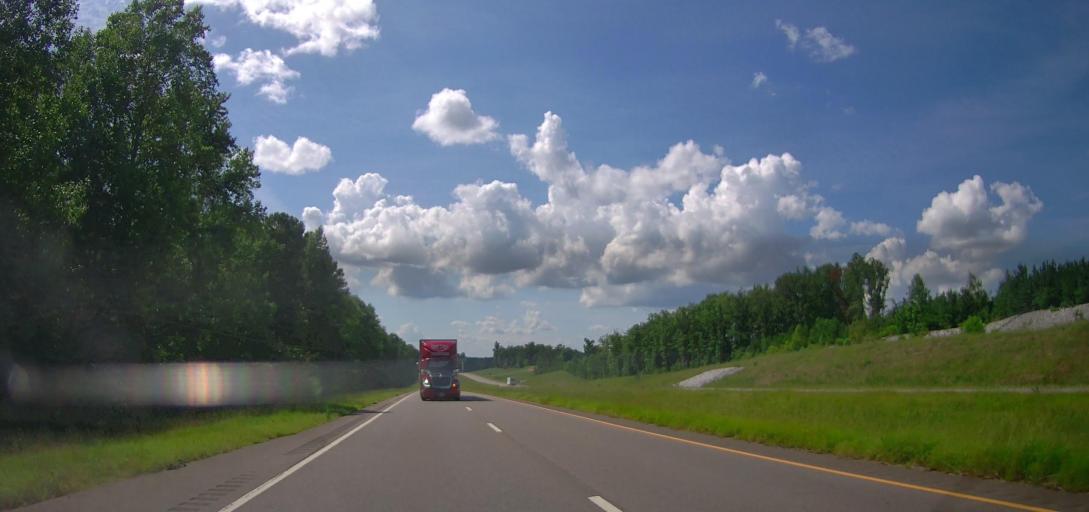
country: US
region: Alabama
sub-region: Pickens County
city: Reform
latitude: 33.3613
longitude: -87.9749
